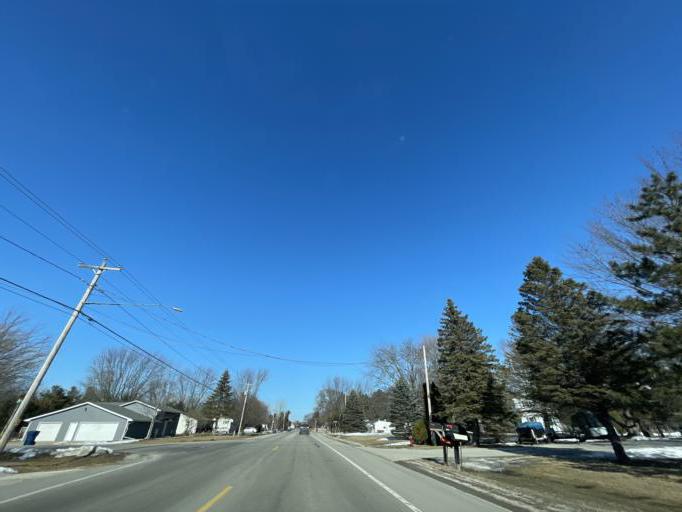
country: US
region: Wisconsin
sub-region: Brown County
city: Suamico
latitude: 44.6225
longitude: -88.0630
